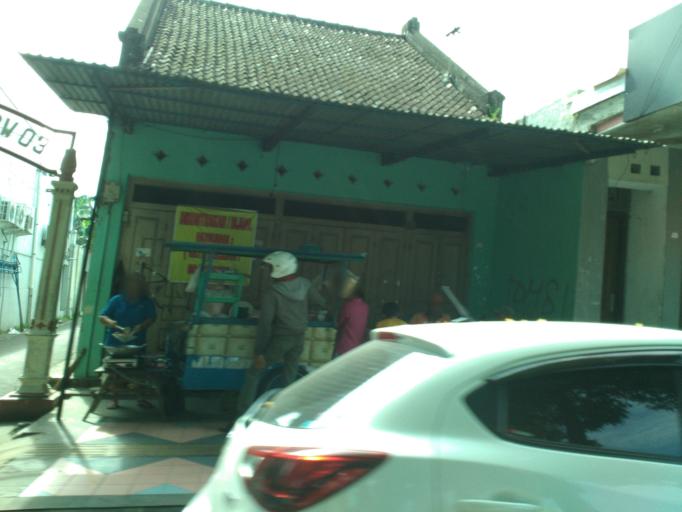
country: ID
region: Central Java
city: Klaten
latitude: -7.7020
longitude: 110.6035
